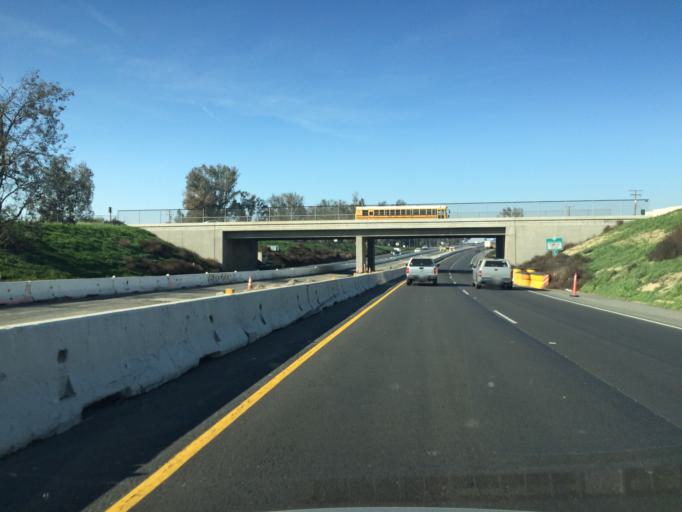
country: US
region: California
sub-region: Tulare County
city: Goshen
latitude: 36.3499
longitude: -119.4264
